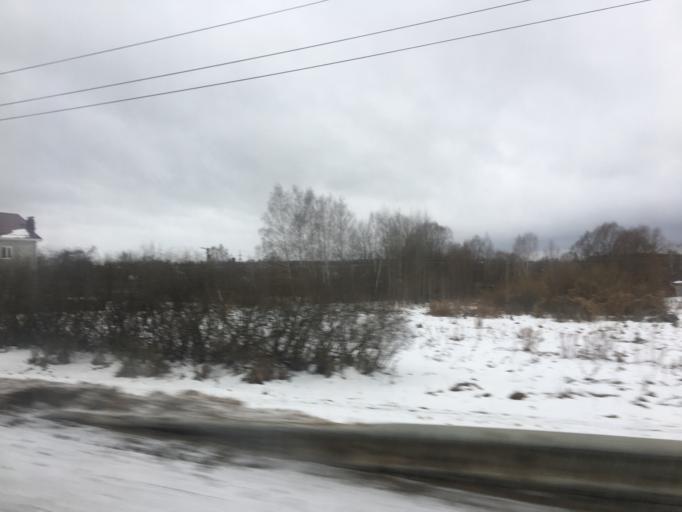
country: RU
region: Tula
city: Pervomayskiy
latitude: 54.0450
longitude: 37.5282
